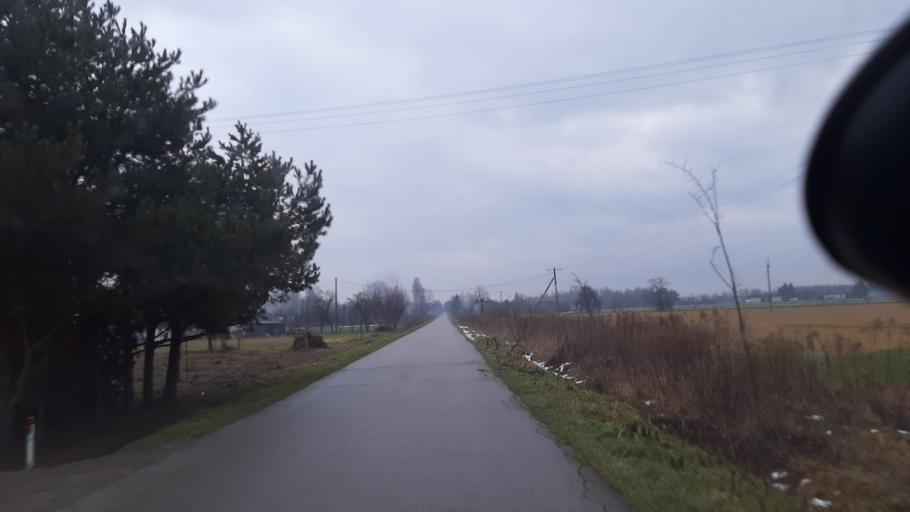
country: PL
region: Lublin Voivodeship
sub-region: Powiat lubelski
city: Lublin
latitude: 51.3389
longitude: 22.5401
